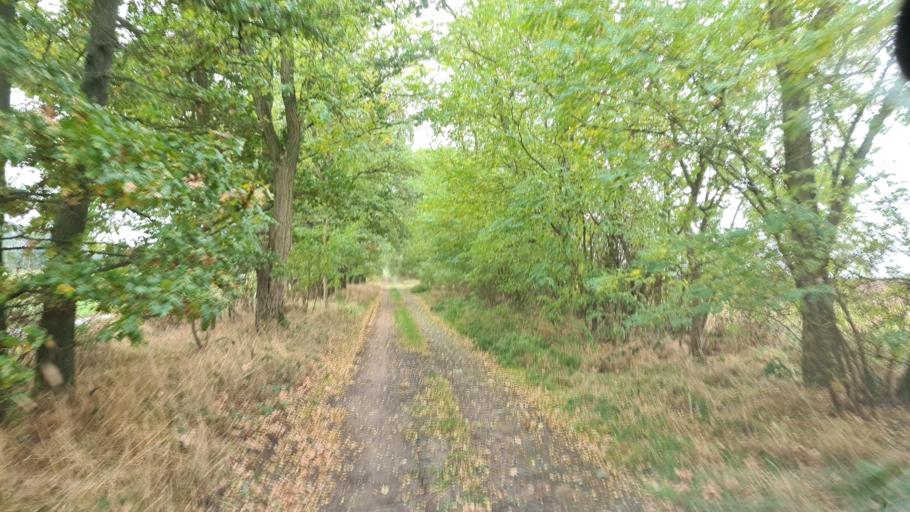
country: DE
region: Brandenburg
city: Furstenwalde
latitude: 52.4173
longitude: 14.0293
